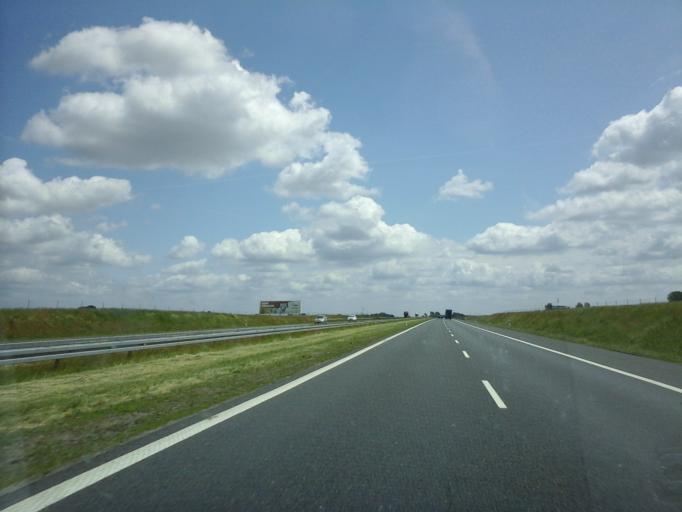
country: PL
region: Lodz Voivodeship
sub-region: Powiat poddebicki
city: Wartkowice
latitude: 51.9840
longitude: 19.0659
